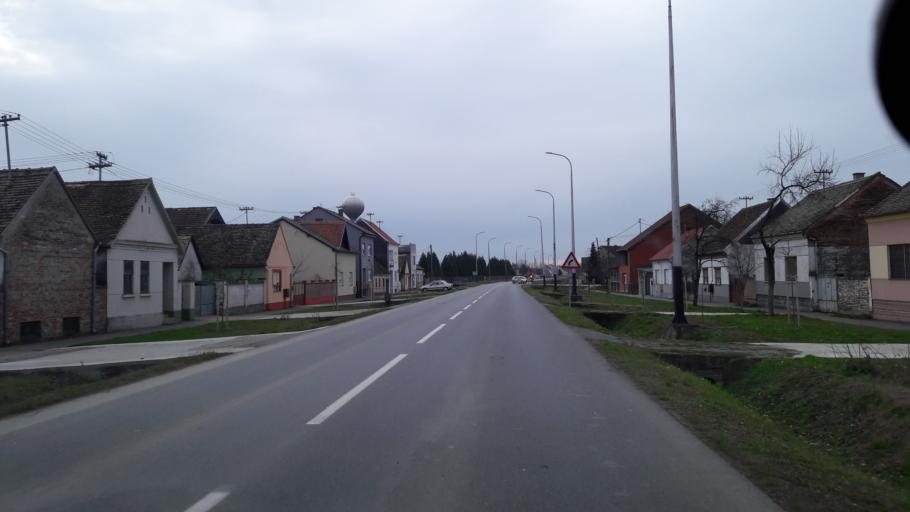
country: HR
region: Osjecko-Baranjska
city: Ovcara
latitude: 45.5161
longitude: 18.5697
